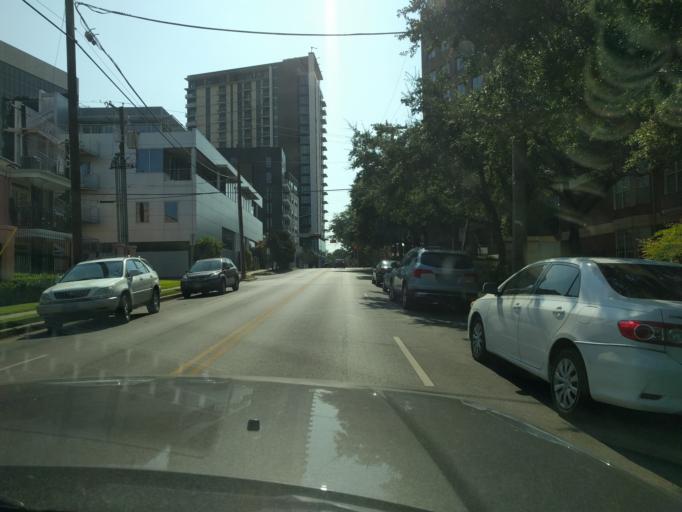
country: US
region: Texas
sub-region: Dallas County
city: Dallas
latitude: 32.8034
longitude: -96.8011
